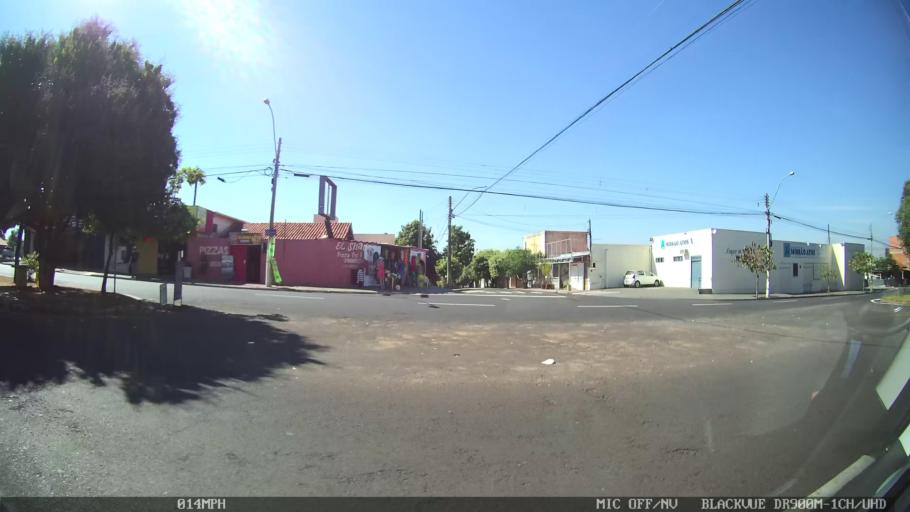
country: BR
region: Sao Paulo
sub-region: Sao Jose Do Rio Preto
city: Sao Jose do Rio Preto
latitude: -20.7533
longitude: -49.4059
